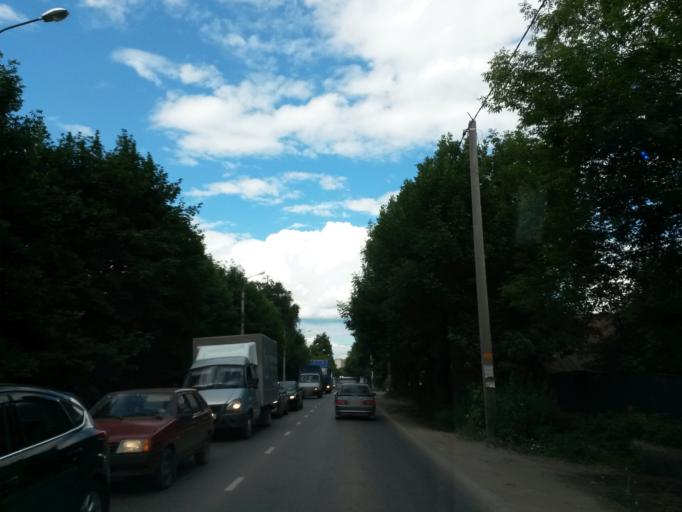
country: RU
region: Ivanovo
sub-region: Gorod Ivanovo
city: Ivanovo
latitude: 56.9894
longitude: 40.9528
